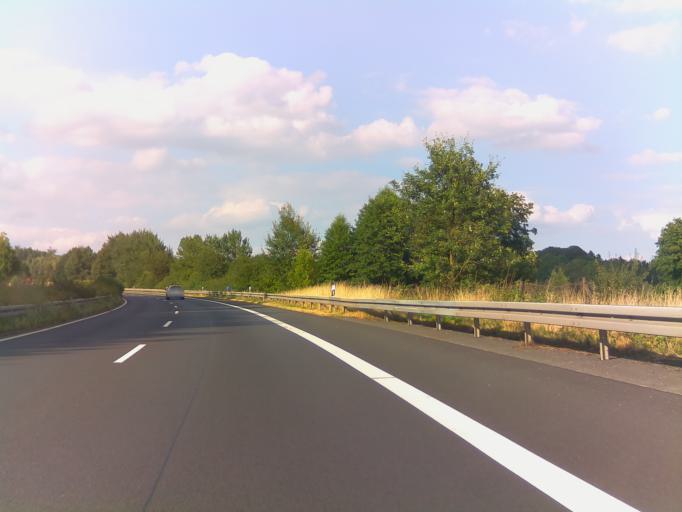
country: DE
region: Hesse
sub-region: Regierungsbezirk Darmstadt
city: Steinau an der Strasse
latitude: 50.3325
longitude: 9.4830
